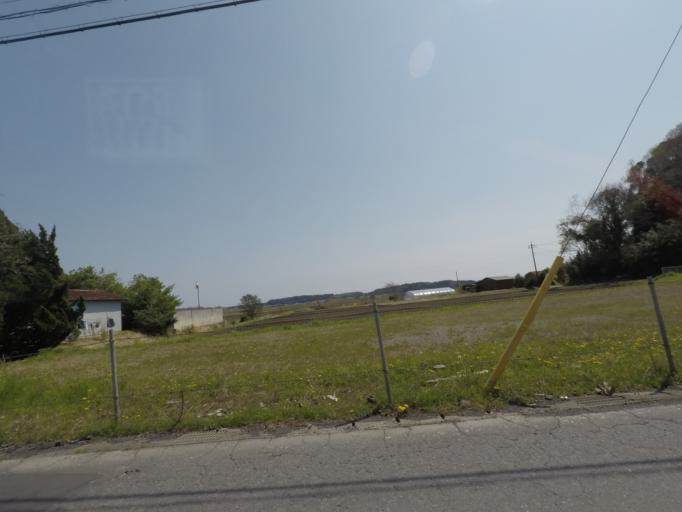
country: JP
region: Chiba
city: Yokaichiba
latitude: 35.7097
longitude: 140.4572
